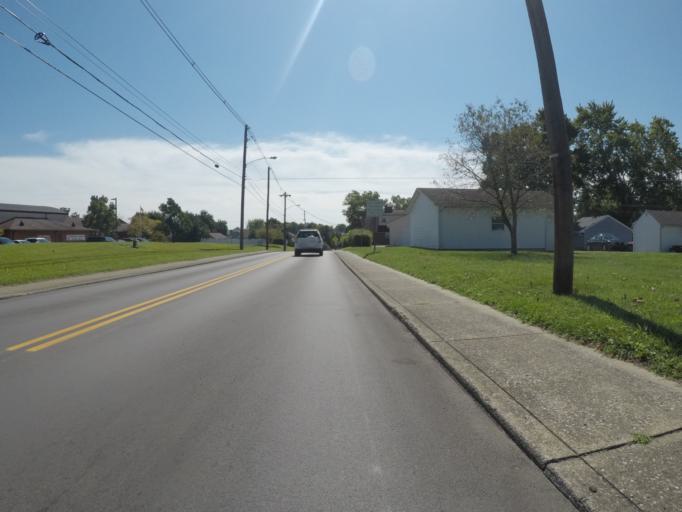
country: US
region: Kentucky
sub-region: Boyd County
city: Ashland
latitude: 38.4552
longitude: -82.6445
